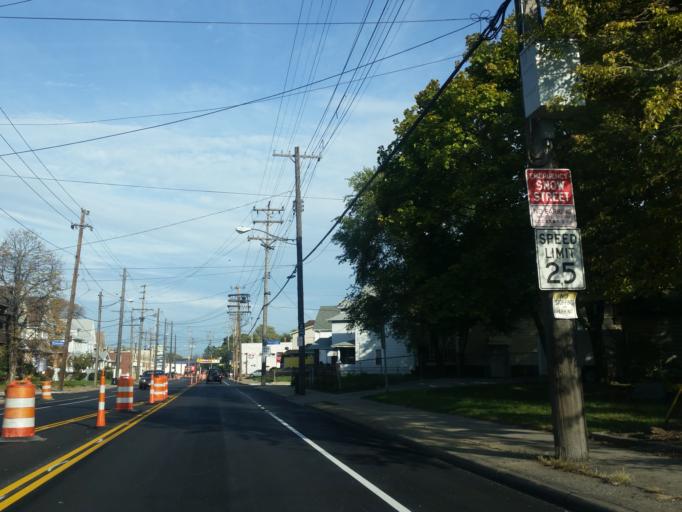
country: US
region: Ohio
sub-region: Cuyahoga County
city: Brooklyn Heights
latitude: 41.4362
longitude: -81.6980
